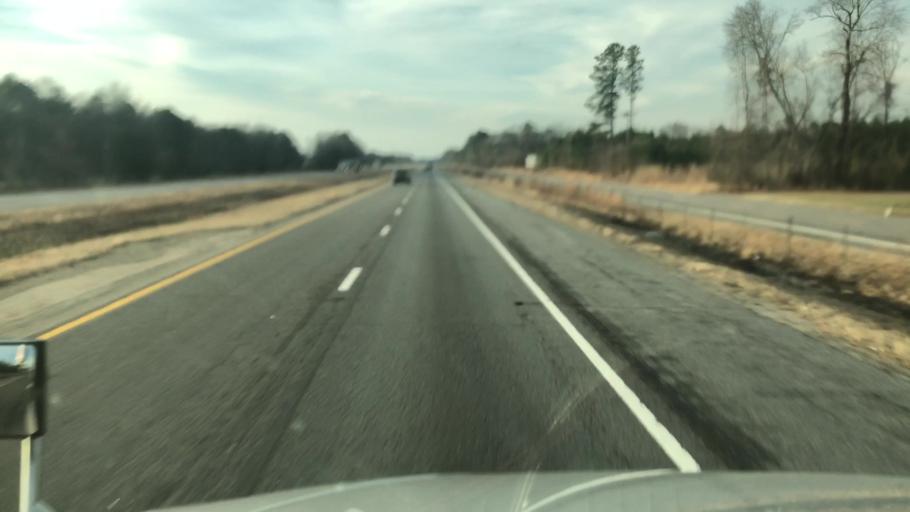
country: US
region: Virginia
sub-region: Sussex County
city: Sussex
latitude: 36.9191
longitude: -77.3968
